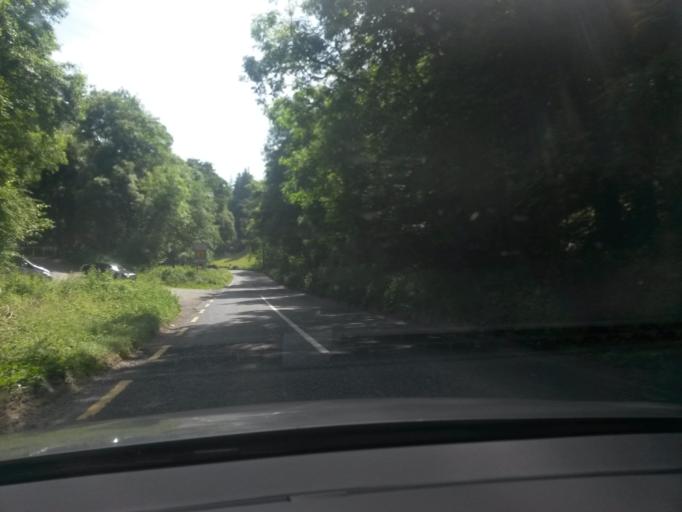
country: IE
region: Leinster
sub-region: Kildare
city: Eadestown
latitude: 53.1805
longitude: -6.5612
